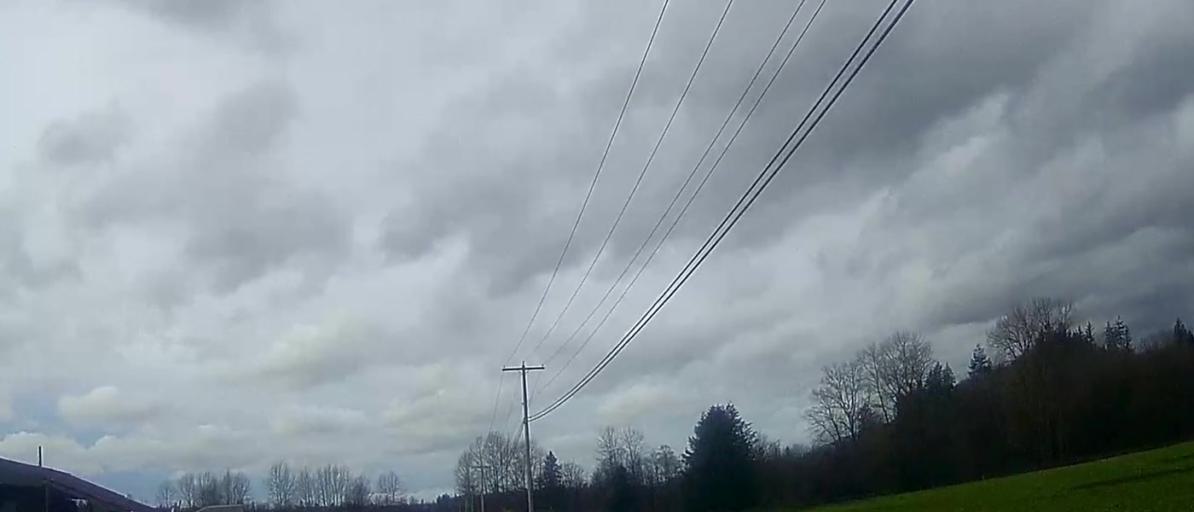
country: US
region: Washington
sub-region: Skagit County
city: Sedro-Woolley
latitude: 48.5835
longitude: -122.2688
